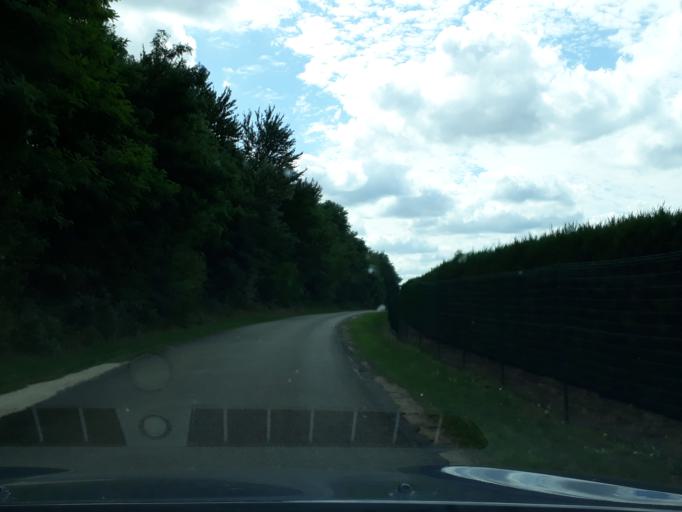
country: FR
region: Centre
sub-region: Departement du Loiret
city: Saint-Cyr-en-Val
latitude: 47.8500
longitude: 1.9762
